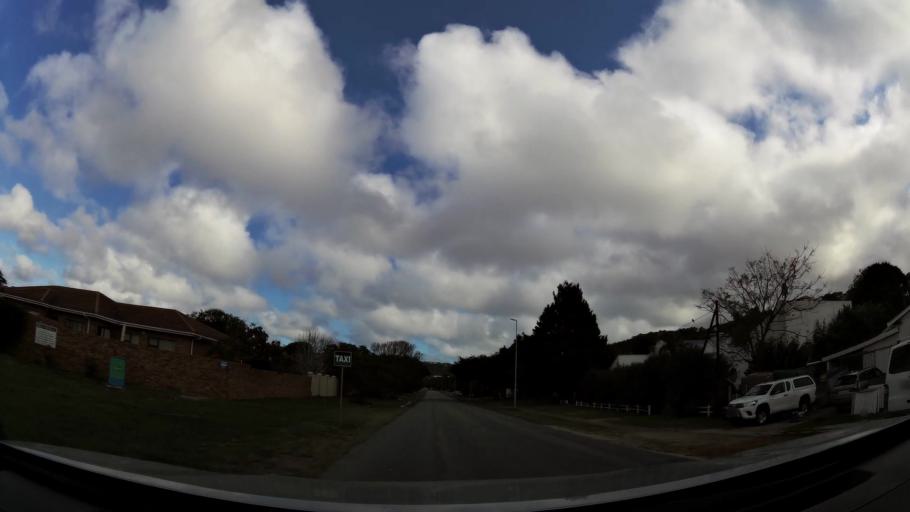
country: ZA
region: Western Cape
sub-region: Eden District Municipality
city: Plettenberg Bay
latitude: -34.0756
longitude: 23.3658
